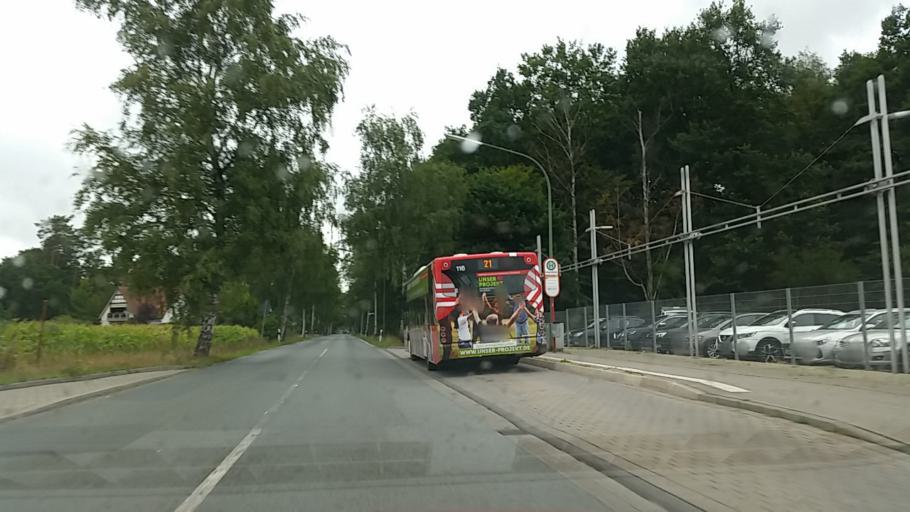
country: DE
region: North Rhine-Westphalia
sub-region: Regierungsbezirk Munster
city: Lotte
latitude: 52.2739
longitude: 7.9561
